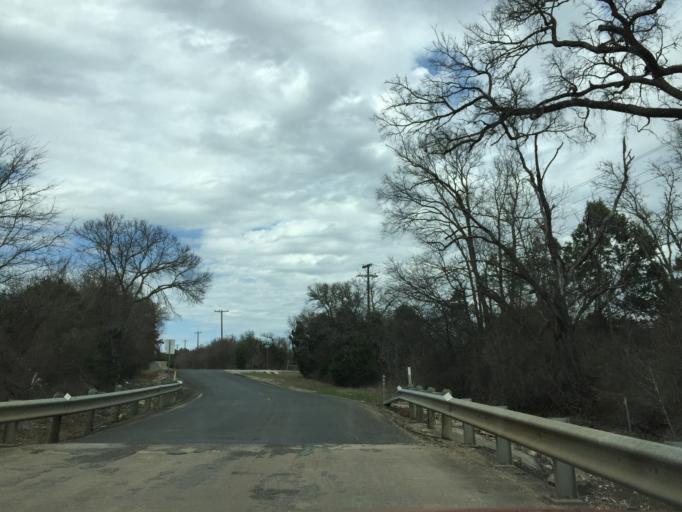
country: US
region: Texas
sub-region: Burnet County
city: Bertram
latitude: 30.7373
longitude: -97.9366
